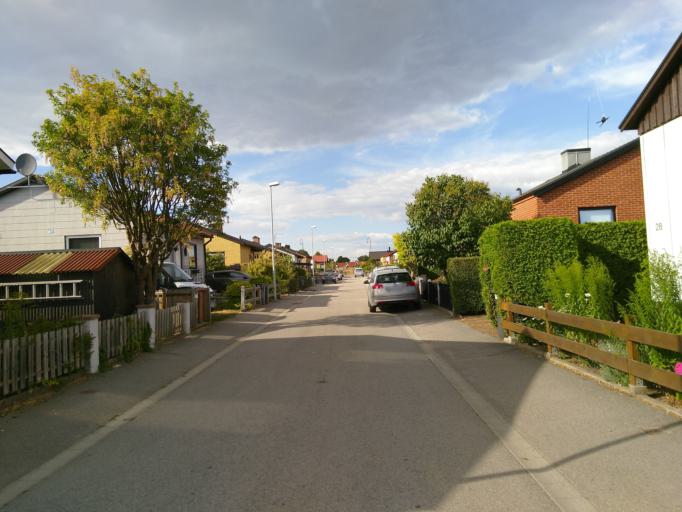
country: SE
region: Skane
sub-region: Landskrona
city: Landskrona
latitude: 55.8773
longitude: 12.8518
